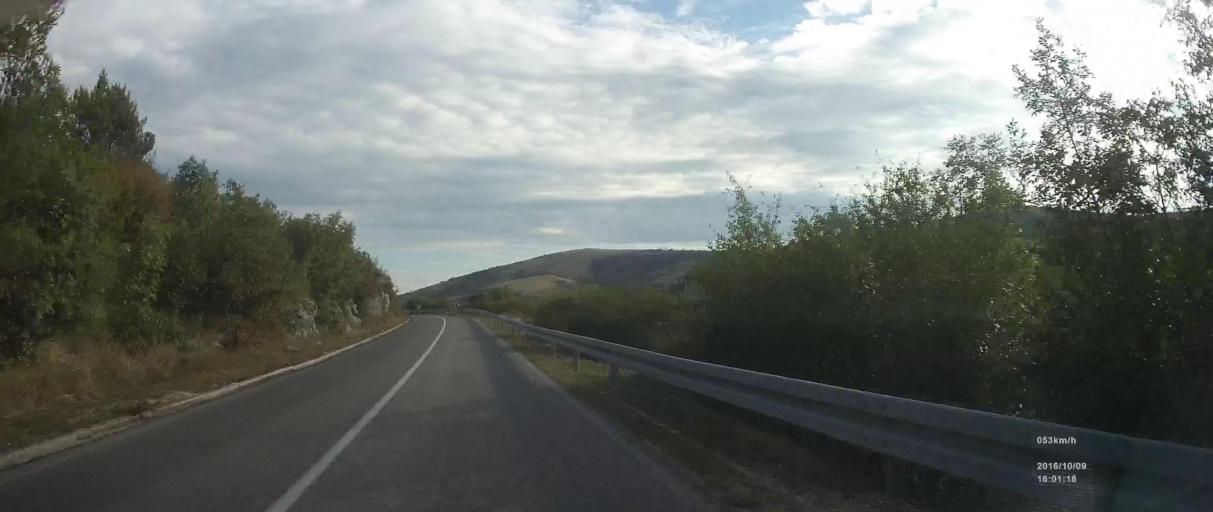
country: HR
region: Splitsko-Dalmatinska
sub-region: Grad Trogir
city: Trogir
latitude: 43.5651
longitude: 16.2453
